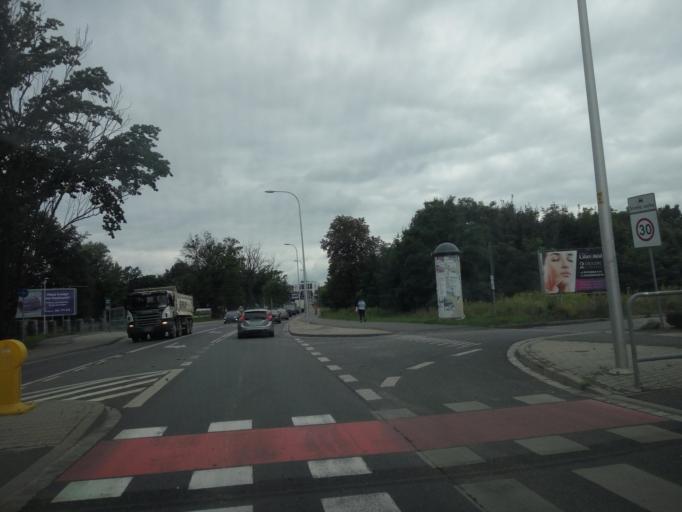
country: PL
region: Lower Silesian Voivodeship
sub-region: Powiat wroclawski
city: Bielany Wroclawskie
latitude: 51.0602
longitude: 17.0022
